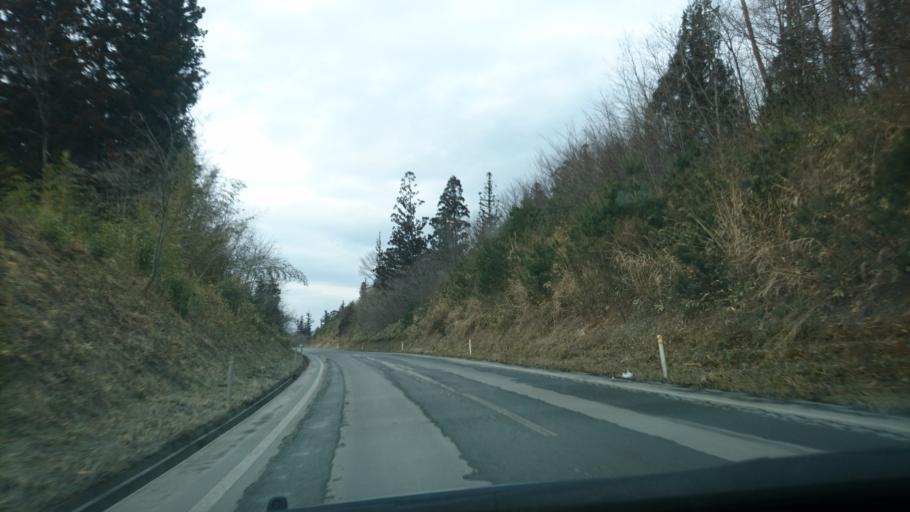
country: JP
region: Iwate
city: Ichinoseki
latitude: 38.9855
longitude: 141.3571
